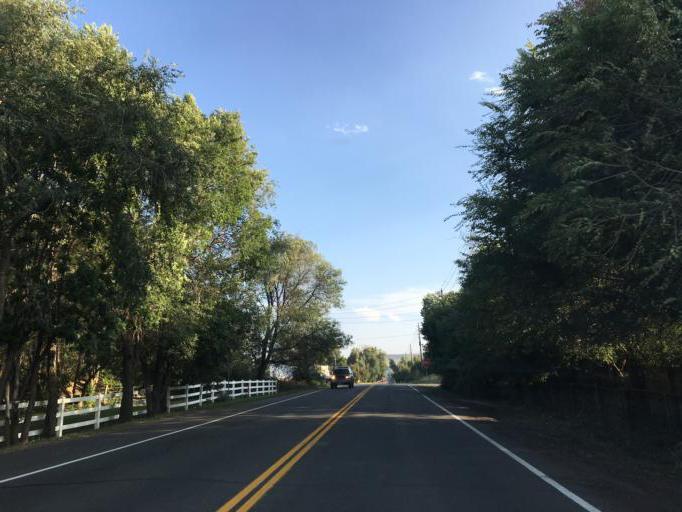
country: US
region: Colorado
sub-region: Jefferson County
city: Applewood
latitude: 39.7916
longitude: -105.1654
